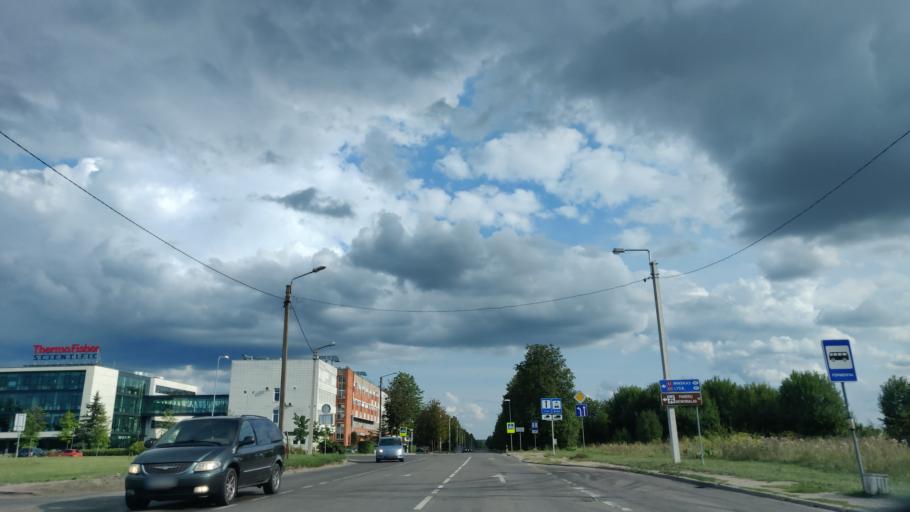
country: LT
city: Baltoji Voke
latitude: 54.6257
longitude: 25.1399
